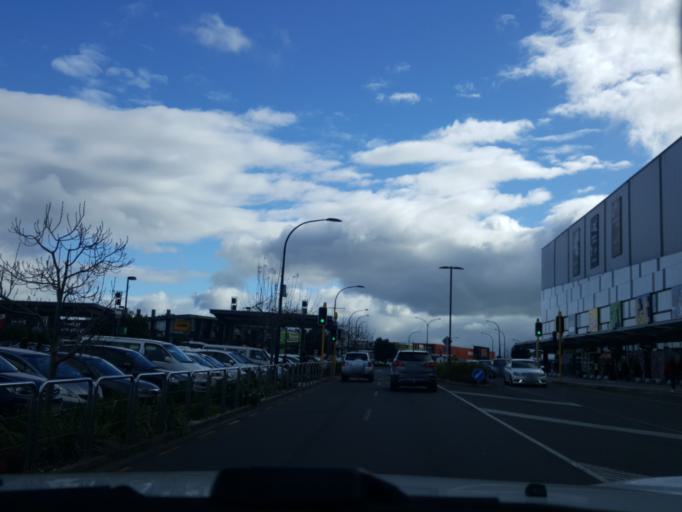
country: NZ
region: Waikato
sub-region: Hamilton City
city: Hamilton
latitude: -37.7494
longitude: 175.2339
